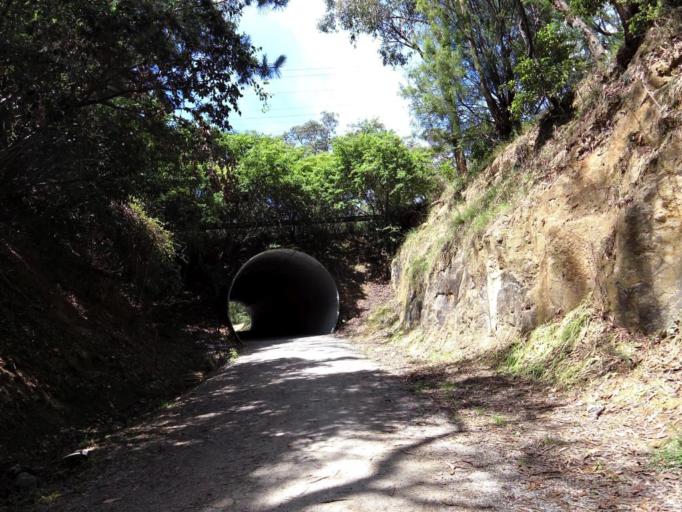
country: AU
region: Victoria
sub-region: Yarra Ranges
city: Mount Evelyn
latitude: -37.7690
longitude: 145.3741
